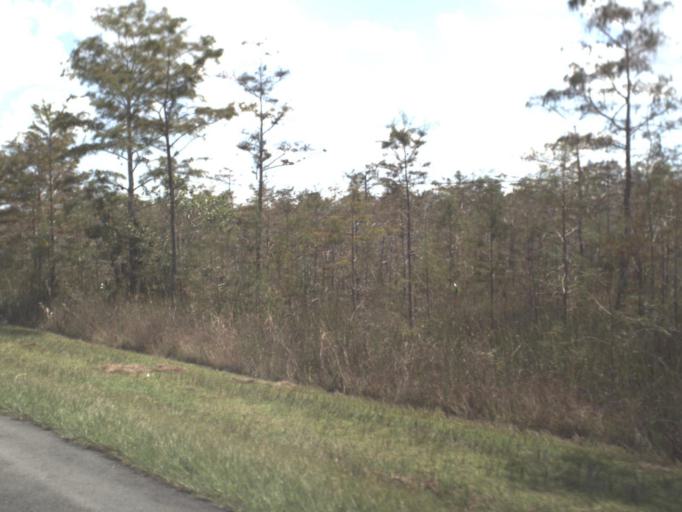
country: US
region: Florida
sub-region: Miami-Dade County
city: Kendall West
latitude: 25.8374
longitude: -80.9104
